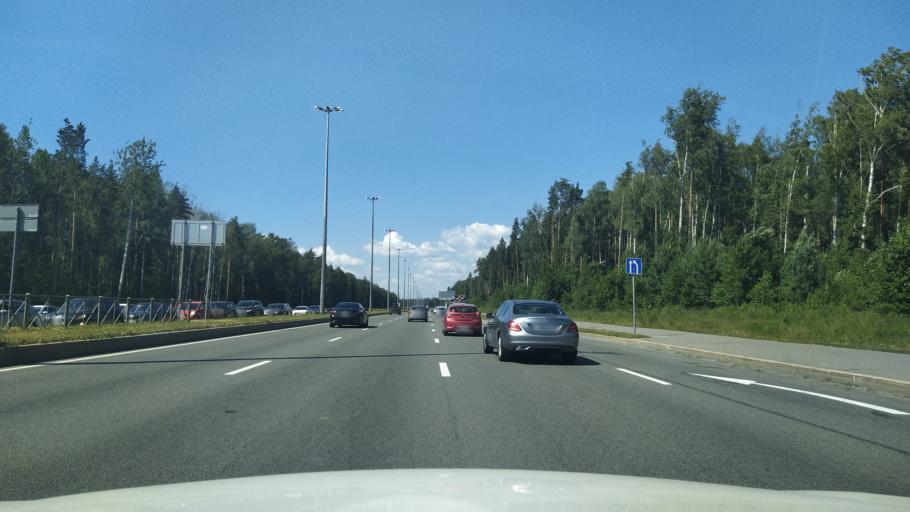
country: RU
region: Leningrad
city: Untolovo
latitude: 60.0533
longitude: 30.2267
